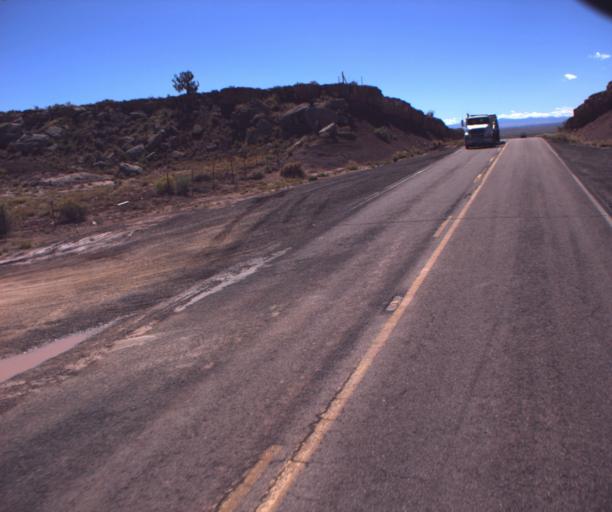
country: US
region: Arizona
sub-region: Apache County
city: Saint Johns
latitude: 34.6516
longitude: -109.2988
